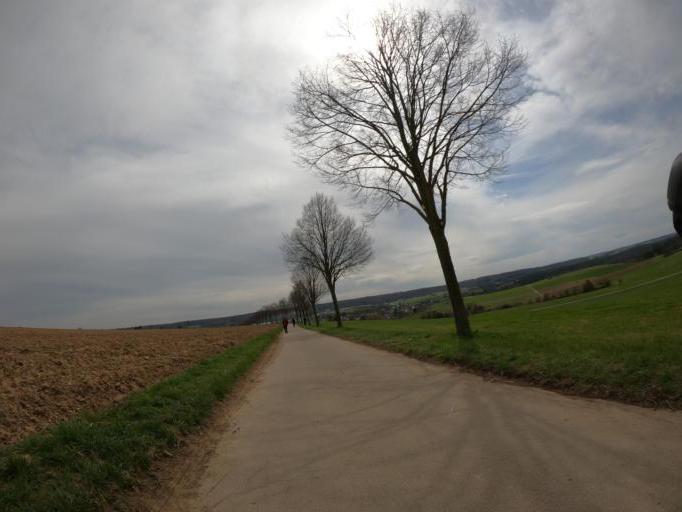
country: DE
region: Baden-Wuerttemberg
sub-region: Regierungsbezirk Stuttgart
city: Waldenbuch
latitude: 48.6514
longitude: 9.1341
